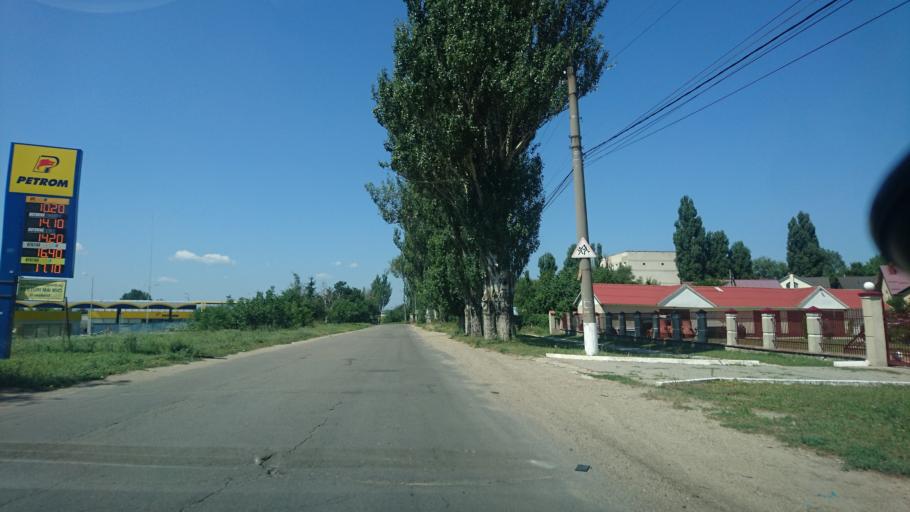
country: MD
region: Laloveni
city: Ialoveni
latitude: 46.9945
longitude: 28.7944
